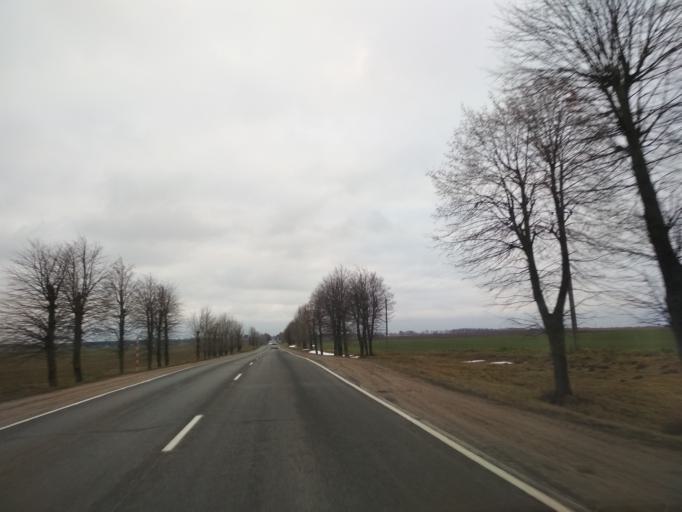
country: BY
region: Minsk
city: Blon'
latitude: 53.5408
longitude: 28.1651
